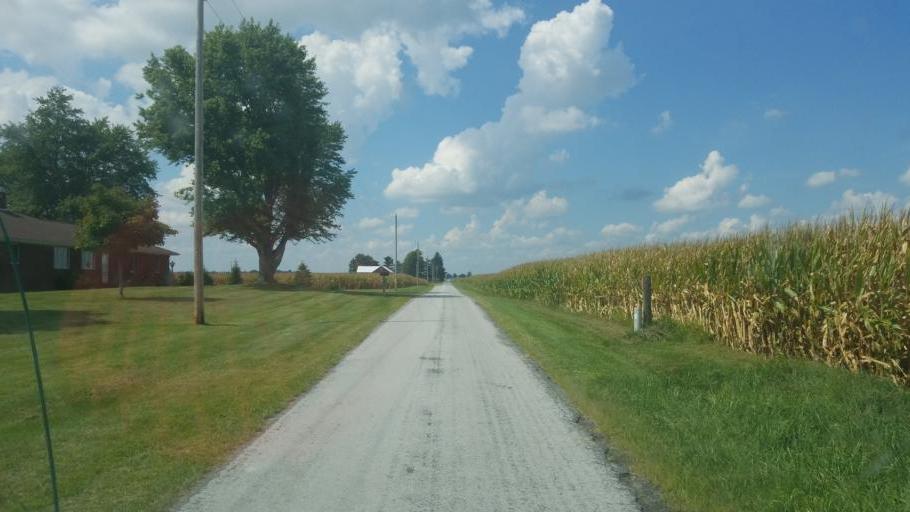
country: US
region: Ohio
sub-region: Hardin County
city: Ada
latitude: 40.7617
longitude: -83.7247
